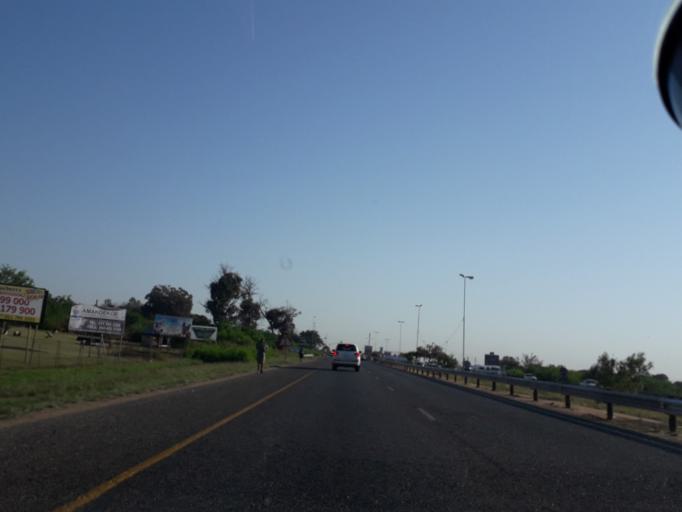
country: ZA
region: Gauteng
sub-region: City of Johannesburg Metropolitan Municipality
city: Roodepoort
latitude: -26.0844
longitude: 27.9303
